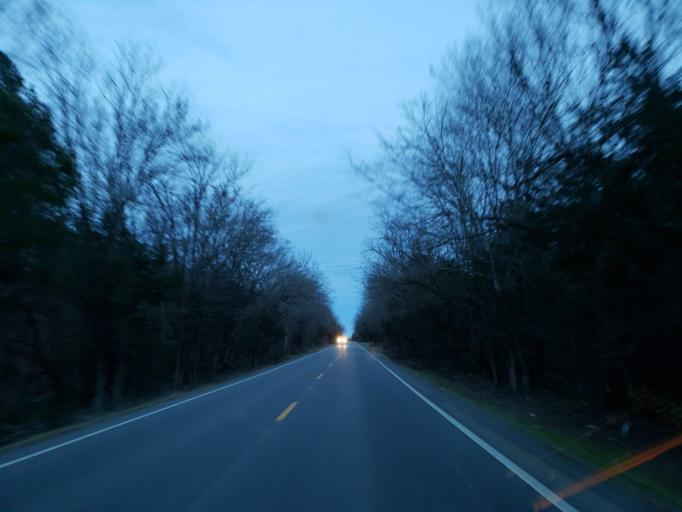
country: US
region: Alabama
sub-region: Sumter County
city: Livingston
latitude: 32.8105
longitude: -88.2376
